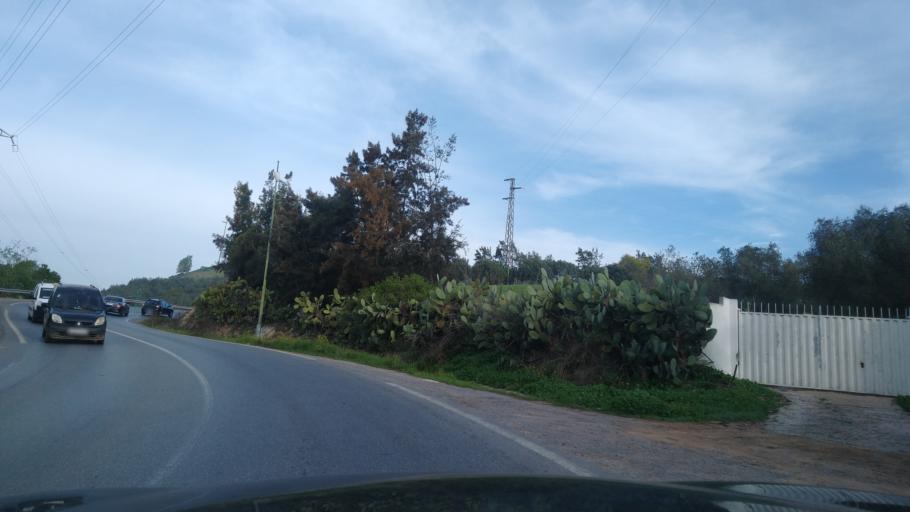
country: MA
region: Rabat-Sale-Zemmour-Zaer
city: Sale
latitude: 33.9915
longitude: -6.7614
